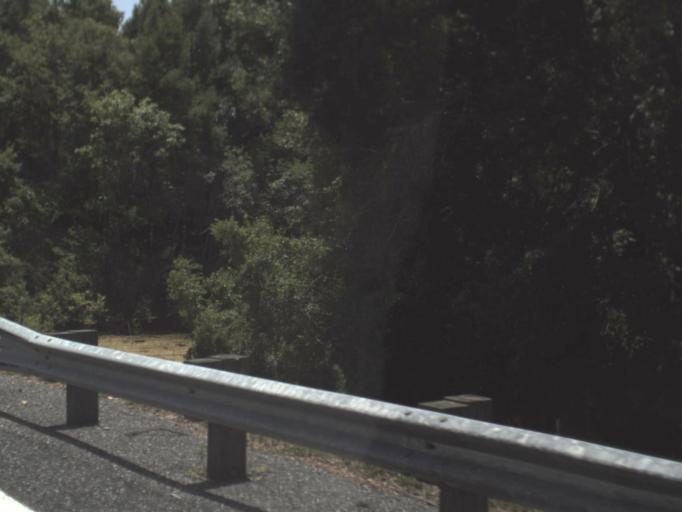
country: US
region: Florida
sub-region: Taylor County
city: Steinhatchee
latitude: 29.6828
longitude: -83.2633
